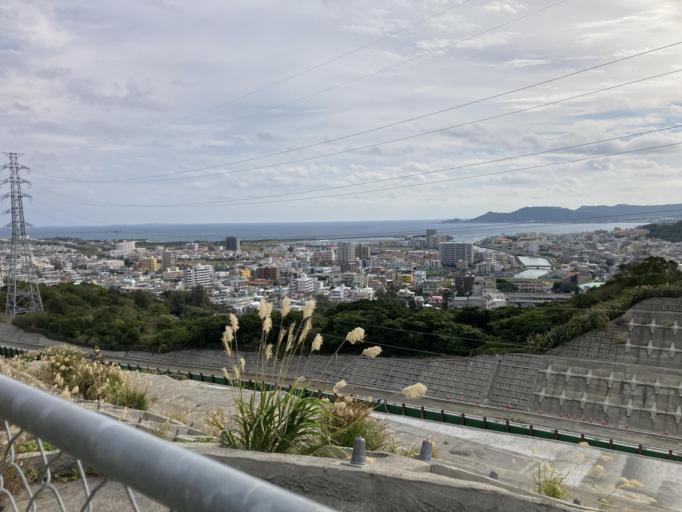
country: JP
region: Okinawa
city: Ginowan
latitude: 26.2063
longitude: 127.7497
